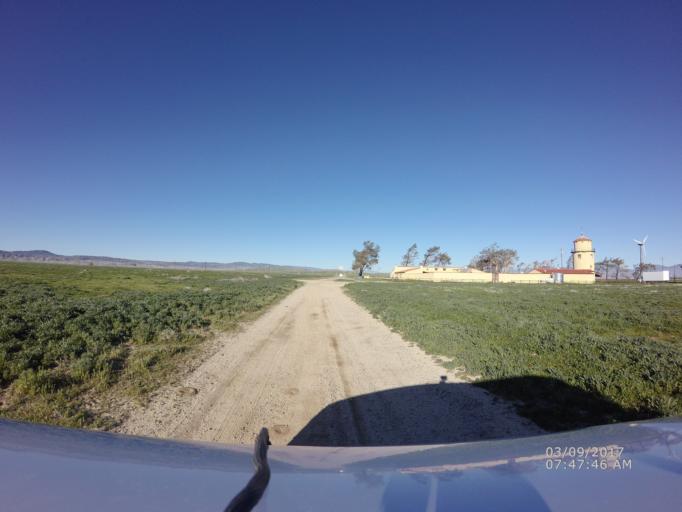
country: US
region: California
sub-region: Los Angeles County
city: Leona Valley
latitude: 34.7544
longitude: -118.3201
